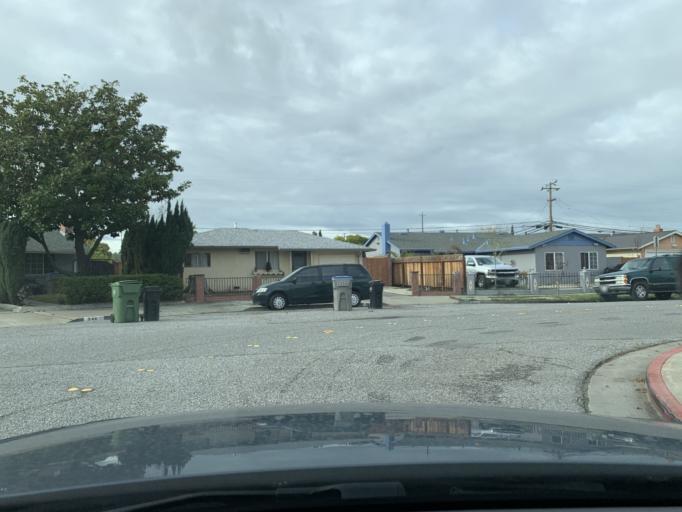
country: US
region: California
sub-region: Santa Clara County
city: Alum Rock
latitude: 37.3493
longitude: -121.8323
